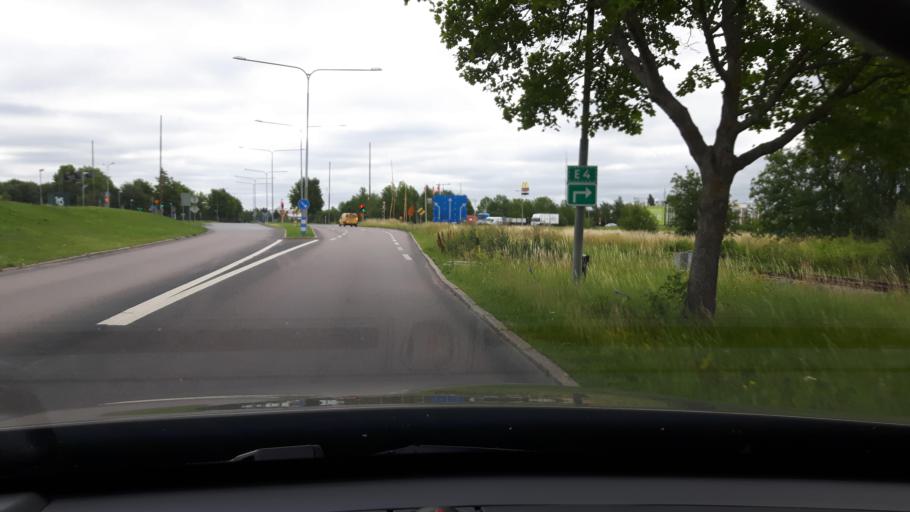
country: SE
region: Uppsala
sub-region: Uppsala Kommun
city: Uppsala
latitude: 59.8581
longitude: 17.6754
